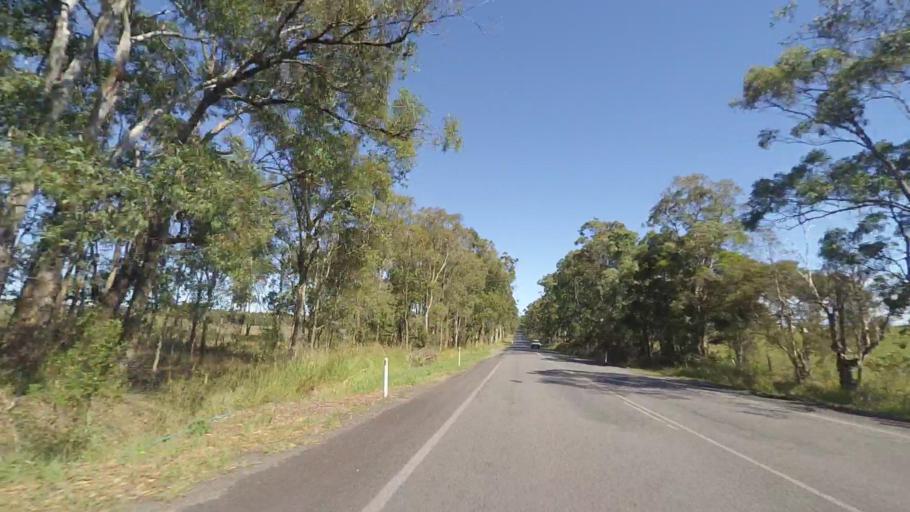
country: AU
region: New South Wales
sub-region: Great Lakes
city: Hawks Nest
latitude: -32.6284
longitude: 152.1334
